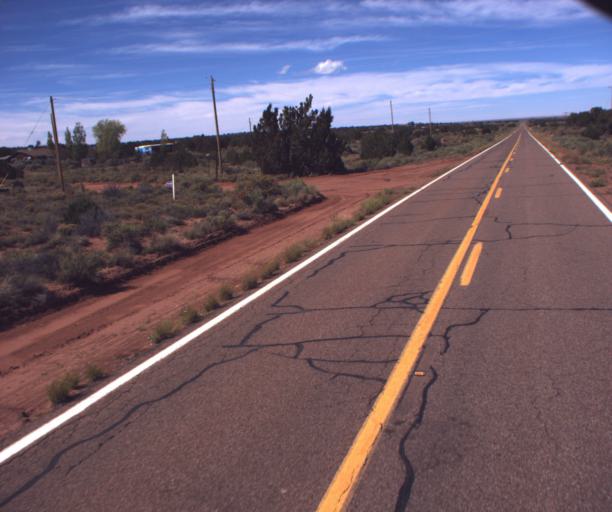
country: US
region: Arizona
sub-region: Apache County
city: Saint Johns
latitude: 34.6009
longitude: -109.6523
